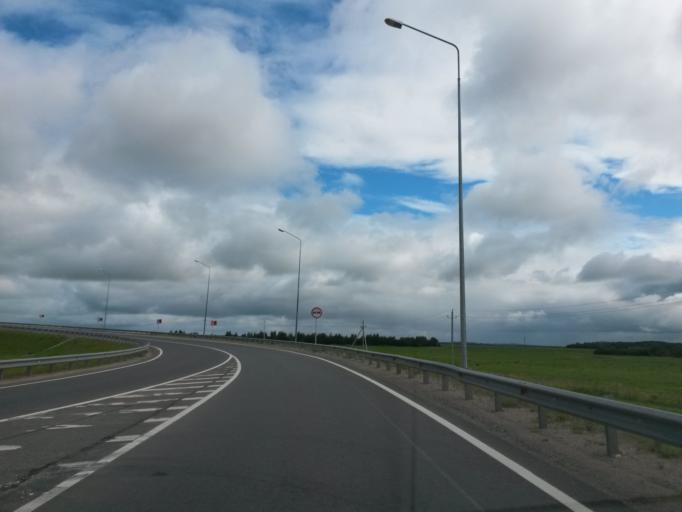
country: RU
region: Jaroslavl
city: Yaroslavl
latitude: 57.7369
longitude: 39.8988
